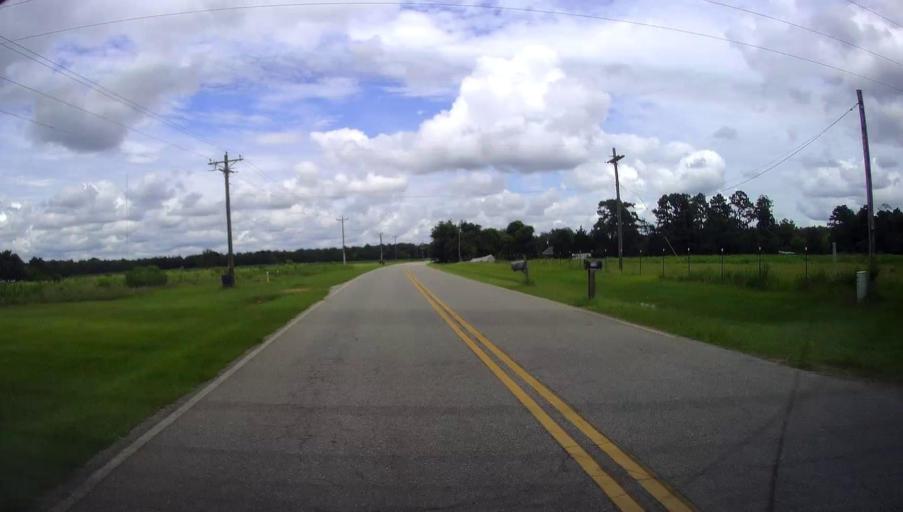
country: US
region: Georgia
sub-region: Peach County
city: Byron
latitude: 32.5630
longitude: -83.7535
